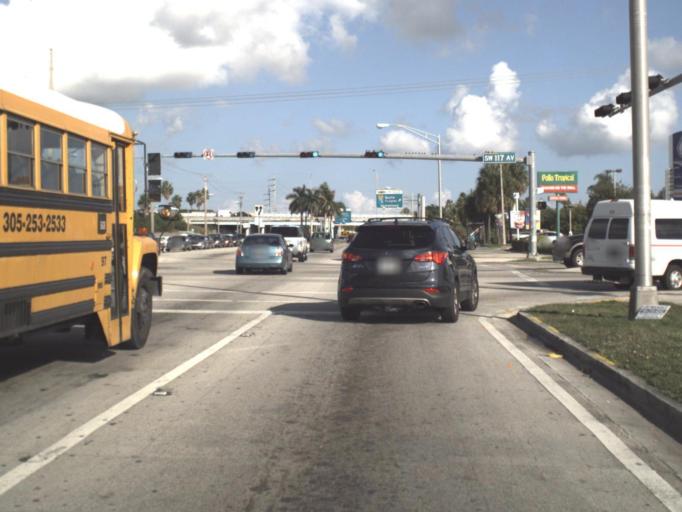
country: US
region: Florida
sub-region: Miami-Dade County
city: Richmond Heights
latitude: 25.6272
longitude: -80.3827
